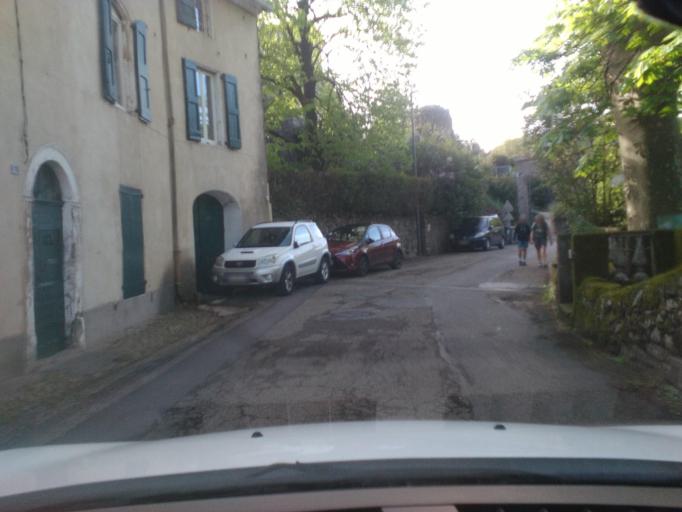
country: FR
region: Languedoc-Roussillon
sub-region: Departement du Gard
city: Lasalle
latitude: 44.0499
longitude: 3.8421
